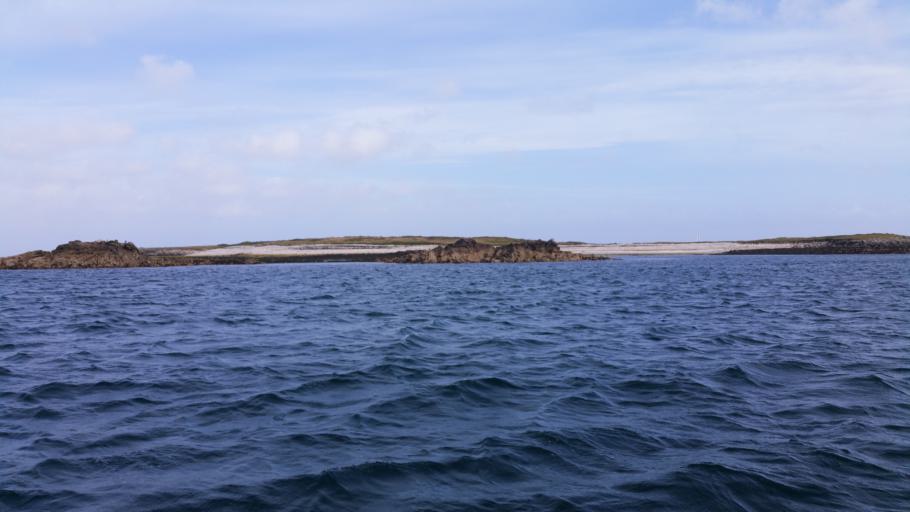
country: FR
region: Brittany
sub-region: Departement du Finistere
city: Le Conquet
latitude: 48.4046
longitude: -4.9539
